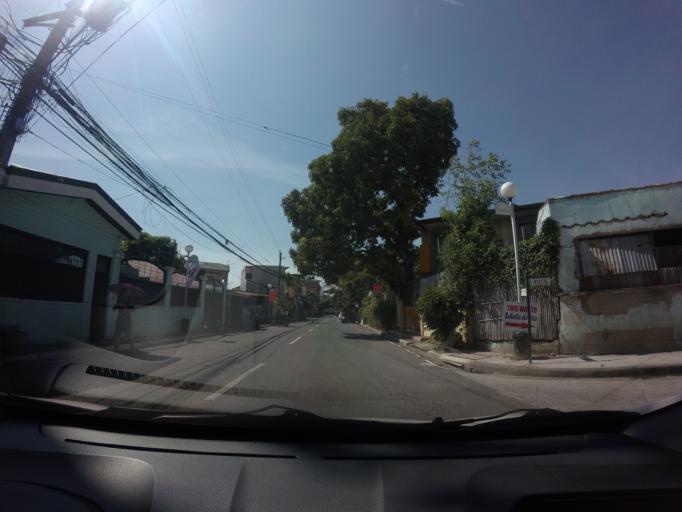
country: PH
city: Sambayanihan People's Village
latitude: 14.4423
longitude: 120.9941
